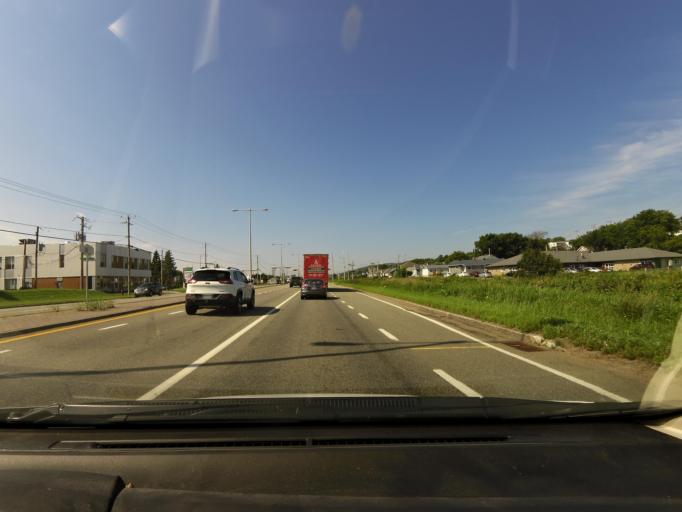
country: CA
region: Quebec
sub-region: Capitale-Nationale
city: Chateau-Richer
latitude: 46.9209
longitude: -71.0763
